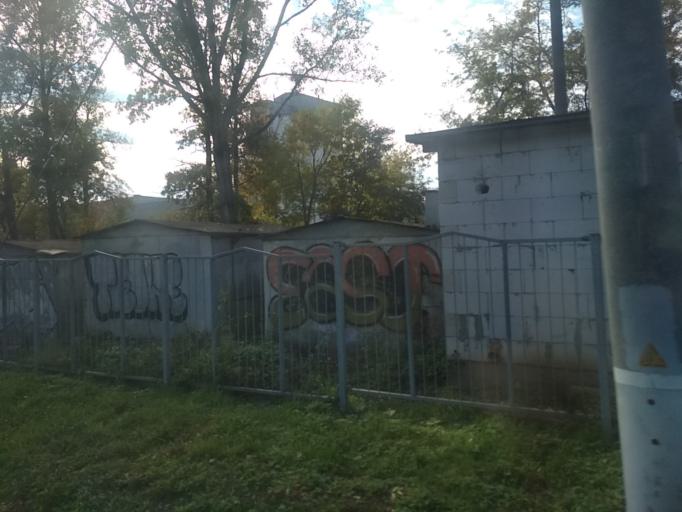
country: BY
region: Minsk
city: Syenitsa
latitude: 53.8439
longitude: 27.5569
